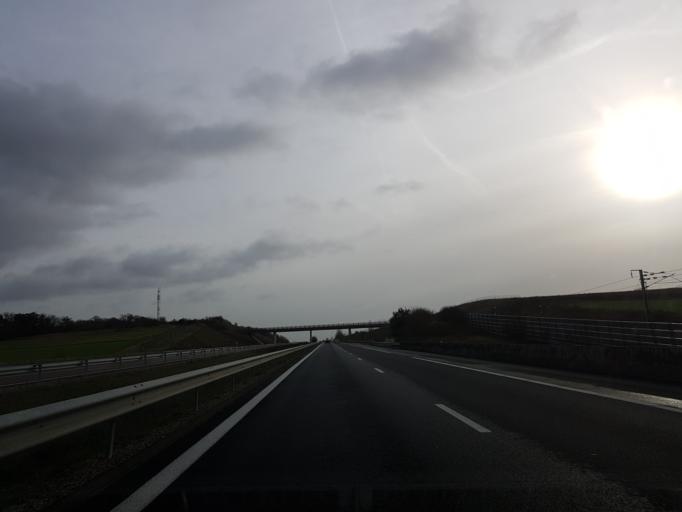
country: FR
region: Bourgogne
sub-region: Departement de l'Yonne
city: Courlon-sur-Yonne
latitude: 48.3444
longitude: 3.1901
